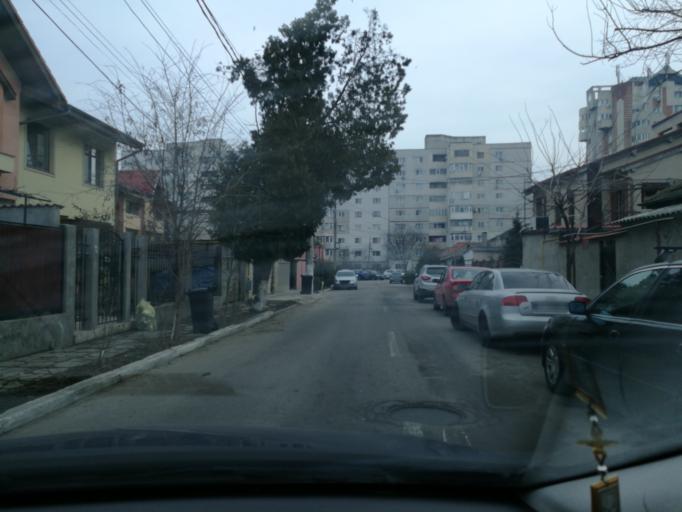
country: RO
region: Constanta
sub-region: Municipiul Constanta
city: Constanta
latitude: 44.1719
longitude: 28.6080
